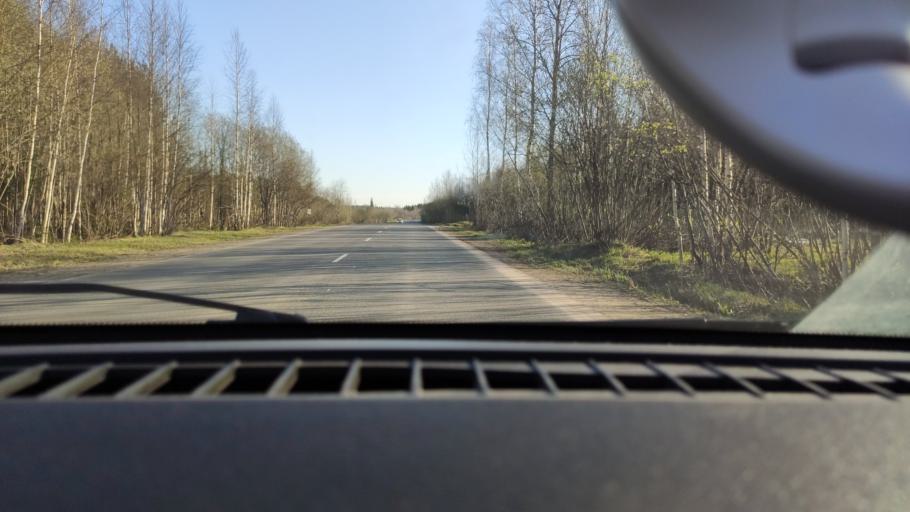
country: RU
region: Perm
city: Polazna
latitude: 58.1193
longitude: 56.4299
